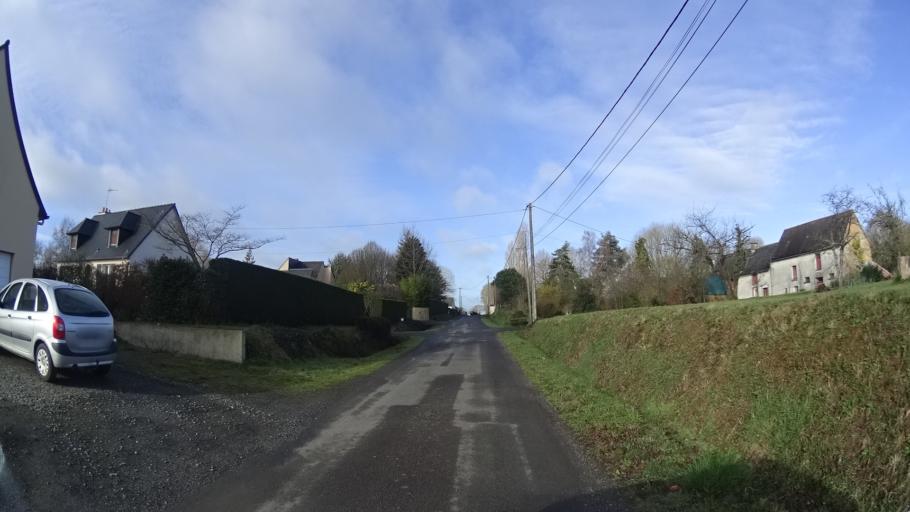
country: FR
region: Brittany
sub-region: Departement d'Ille-et-Vilaine
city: Romille
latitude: 48.2172
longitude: -1.9018
